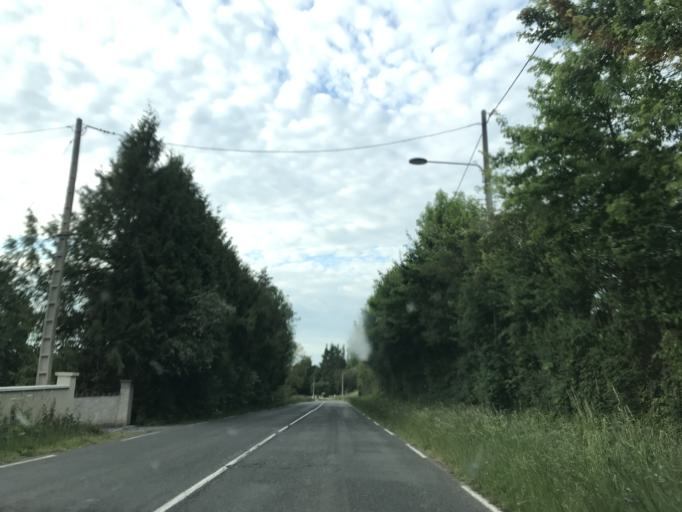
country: FR
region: Auvergne
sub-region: Departement de l'Allier
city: Bellerive-sur-Allier
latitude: 46.0992
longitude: 3.4021
